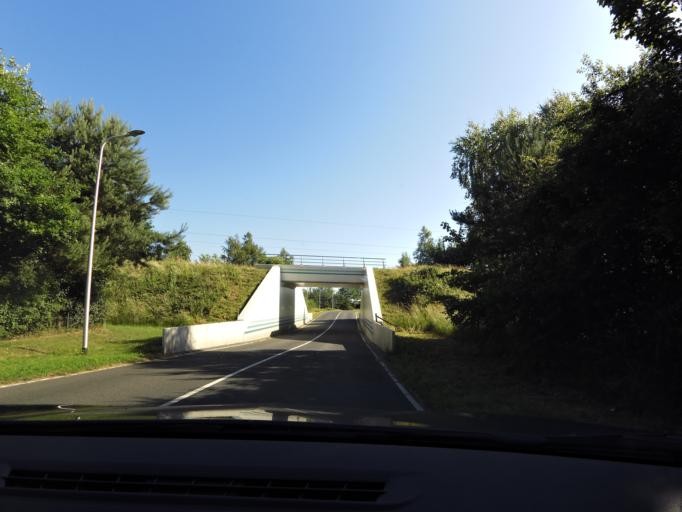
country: NL
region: Overijssel
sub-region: Gemeente Raalte
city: Raalte
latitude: 52.3702
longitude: 6.3992
